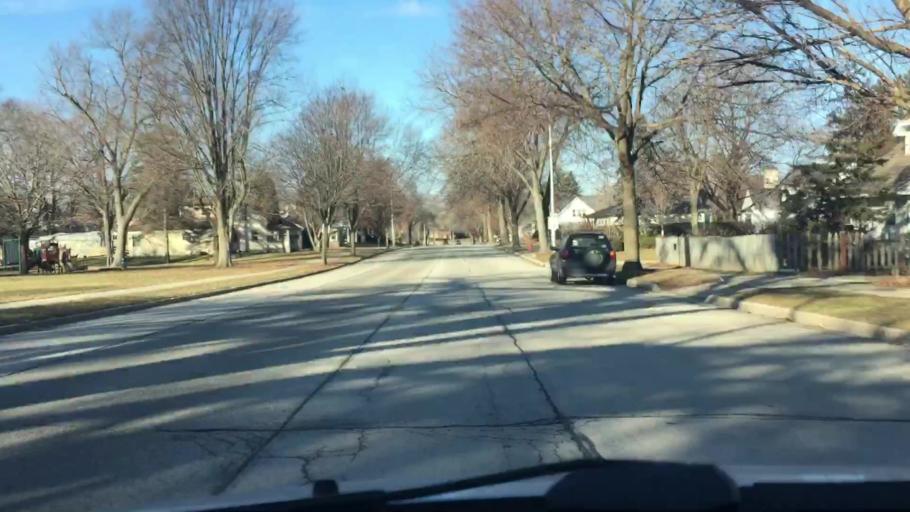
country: US
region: Wisconsin
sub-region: Waukesha County
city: Pewaukee
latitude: 43.0787
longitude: -88.2572
